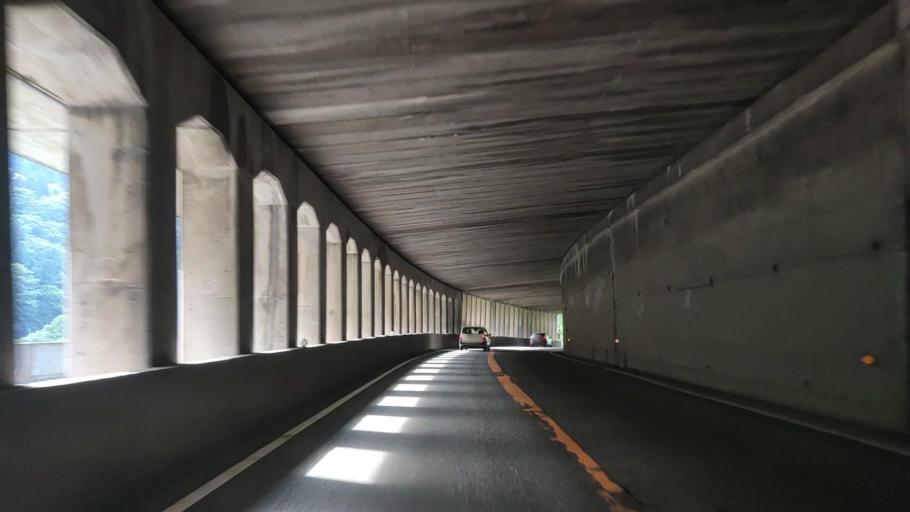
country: JP
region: Toyama
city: Yatsuomachi-higashikumisaka
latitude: 36.4296
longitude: 137.2793
